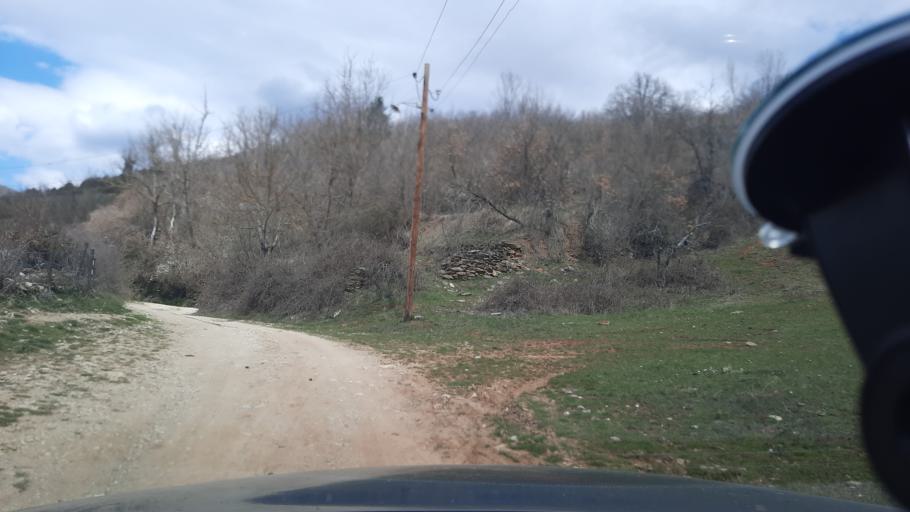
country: MK
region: Demir Hisar
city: Sopotnica
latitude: 41.3020
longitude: 21.1526
